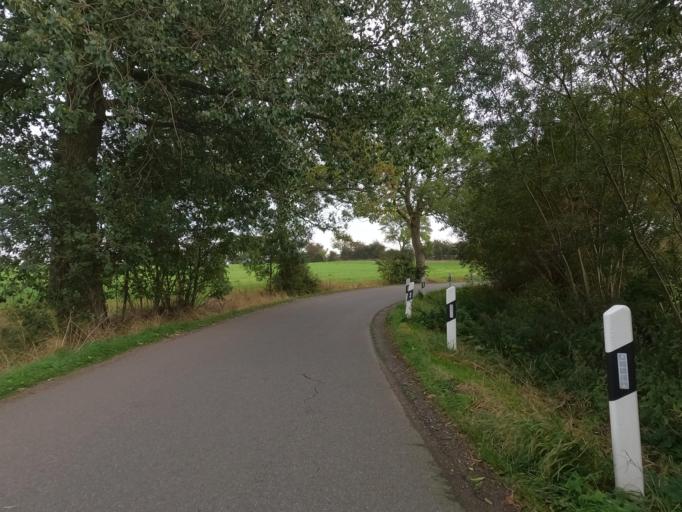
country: DE
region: Schleswig-Holstein
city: Neukirchen
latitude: 54.3471
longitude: 11.0349
